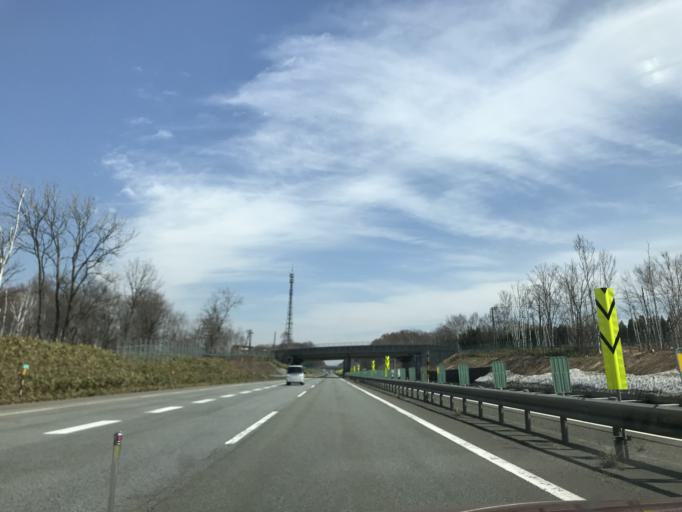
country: JP
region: Hokkaido
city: Iwamizawa
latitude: 43.1768
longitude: 141.7703
